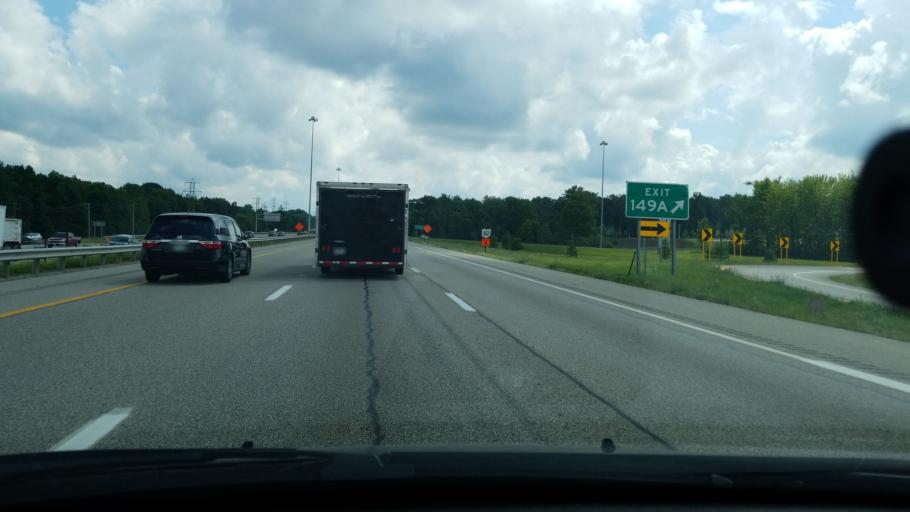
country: US
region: Ohio
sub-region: Cuyahoga County
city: Brecksville
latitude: 41.3155
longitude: -81.6490
